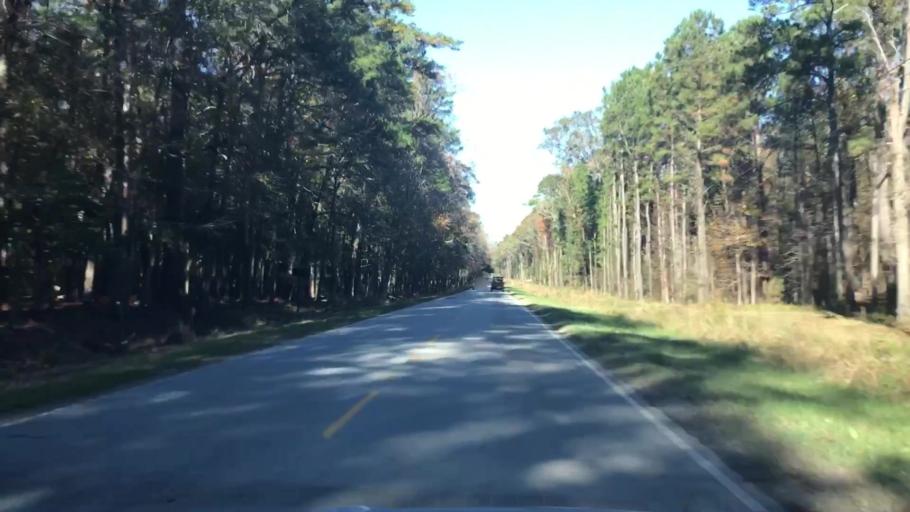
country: US
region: South Carolina
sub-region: Dorchester County
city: Centerville
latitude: 32.9292
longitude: -80.1708
